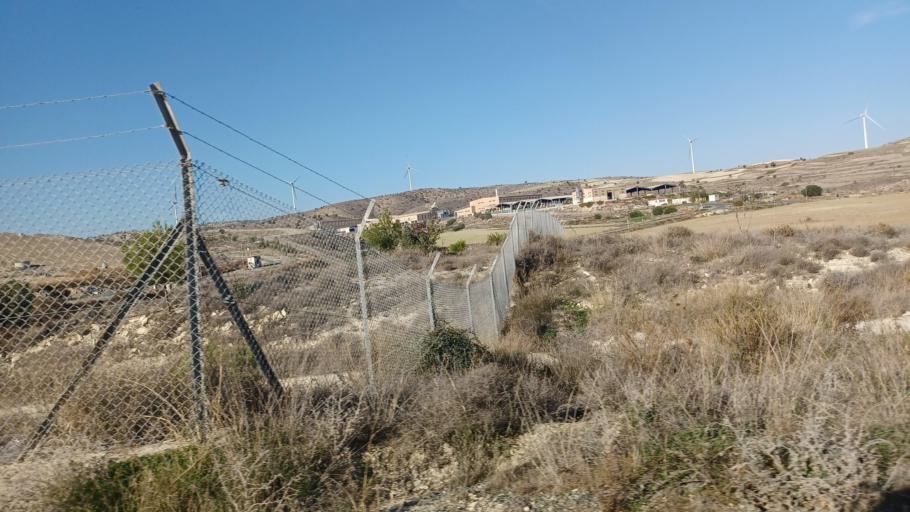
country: CY
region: Larnaka
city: Psevdas
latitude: 34.9641
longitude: 33.5122
